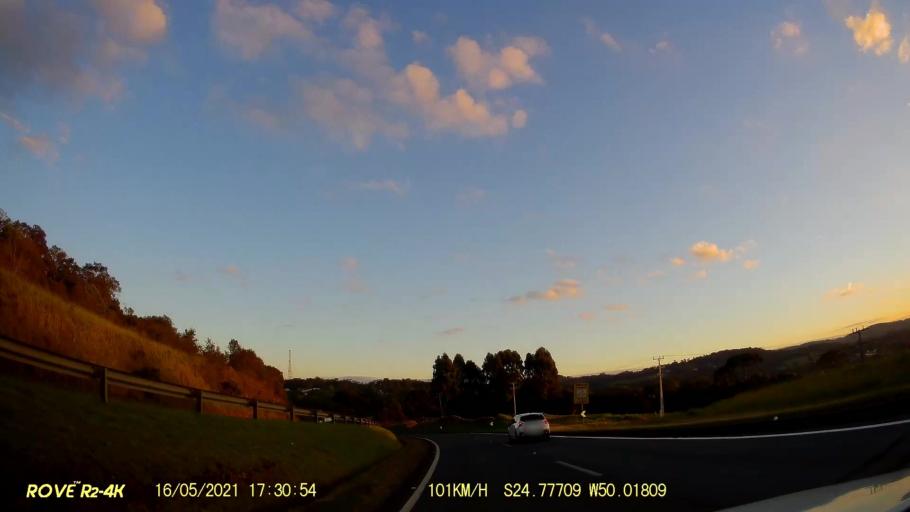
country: BR
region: Parana
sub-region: Castro
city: Castro
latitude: -24.7774
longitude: -50.0183
